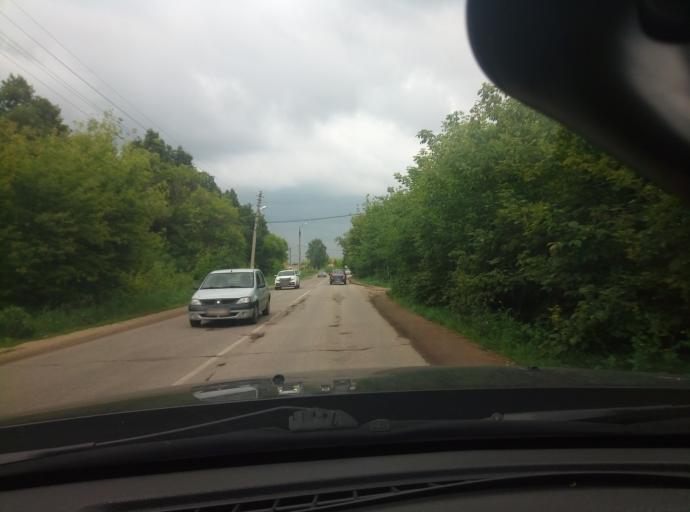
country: RU
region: Tula
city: Kimovsk
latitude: 53.9683
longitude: 38.5482
